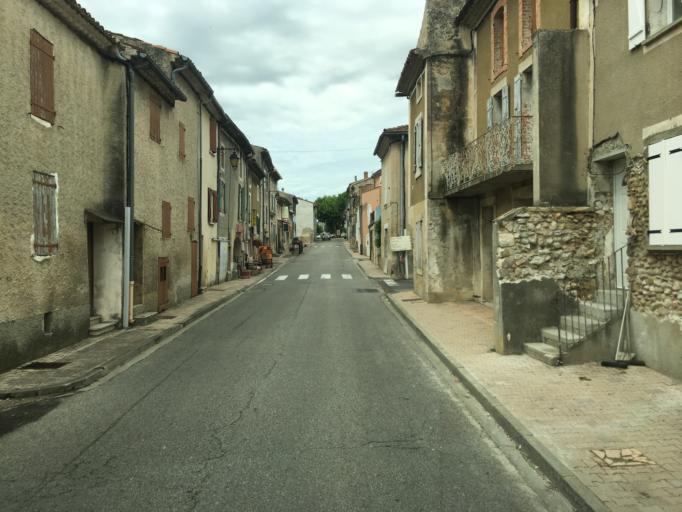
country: FR
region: Provence-Alpes-Cote d'Azur
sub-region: Departement du Vaucluse
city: Visan
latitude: 44.2990
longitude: 5.0111
